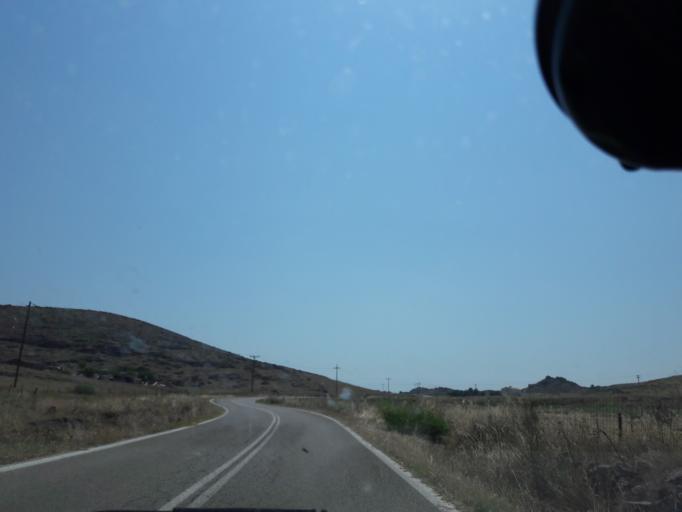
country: GR
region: North Aegean
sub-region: Nomos Lesvou
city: Myrina
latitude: 39.8608
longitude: 25.1470
